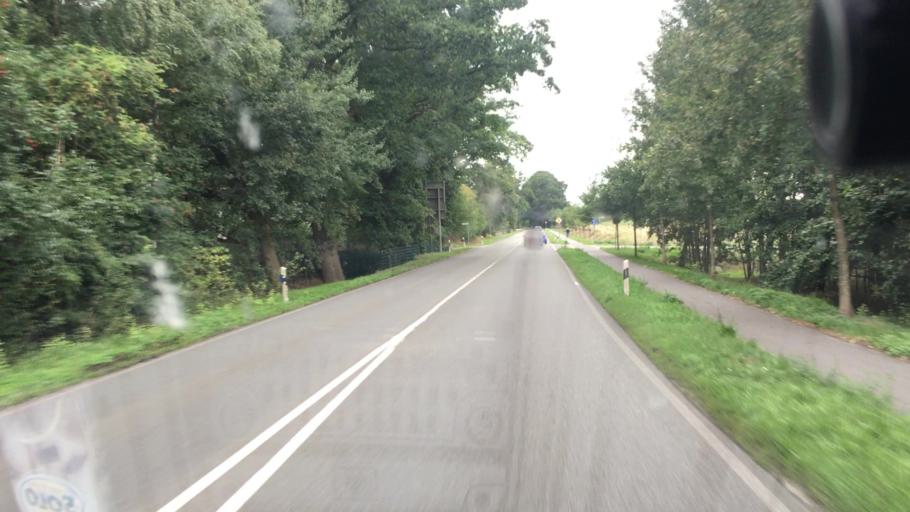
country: DE
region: Lower Saxony
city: Lohne
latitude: 52.6508
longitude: 8.2425
